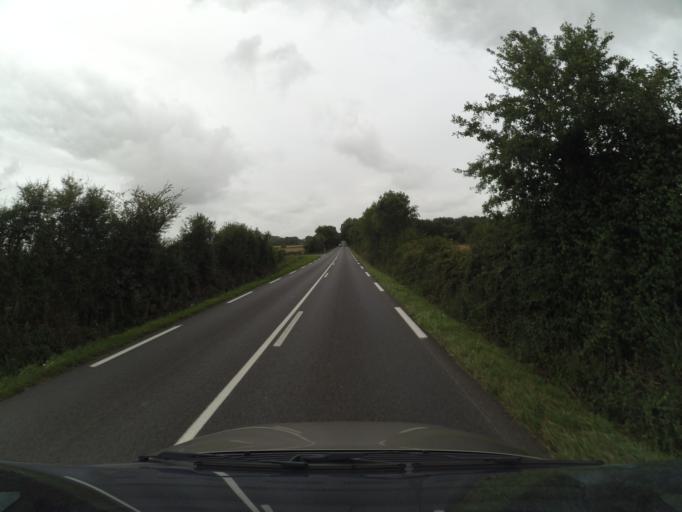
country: FR
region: Pays de la Loire
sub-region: Departement de la Vendee
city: Froidfond
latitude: 46.8748
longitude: -1.7341
